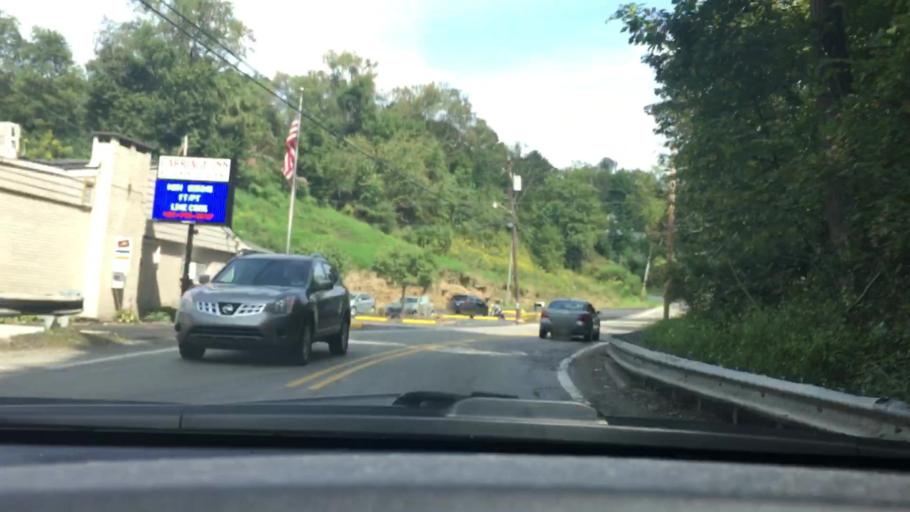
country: US
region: Pennsylvania
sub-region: Allegheny County
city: Versailles
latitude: 40.2847
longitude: -79.8440
